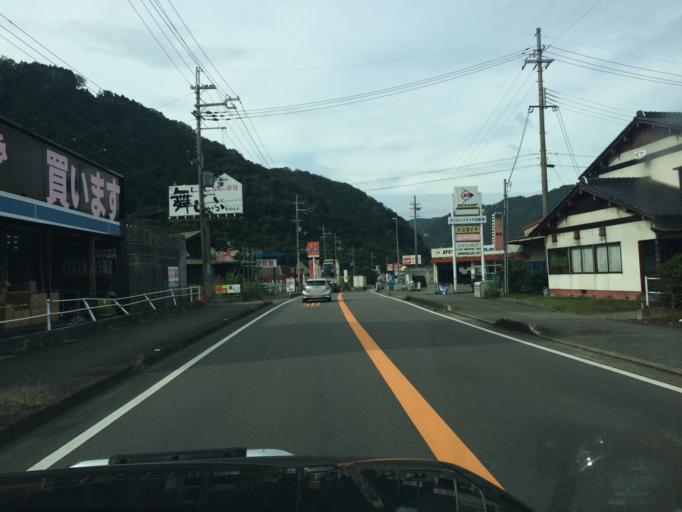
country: JP
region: Hyogo
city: Toyooka
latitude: 35.3483
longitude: 134.8369
